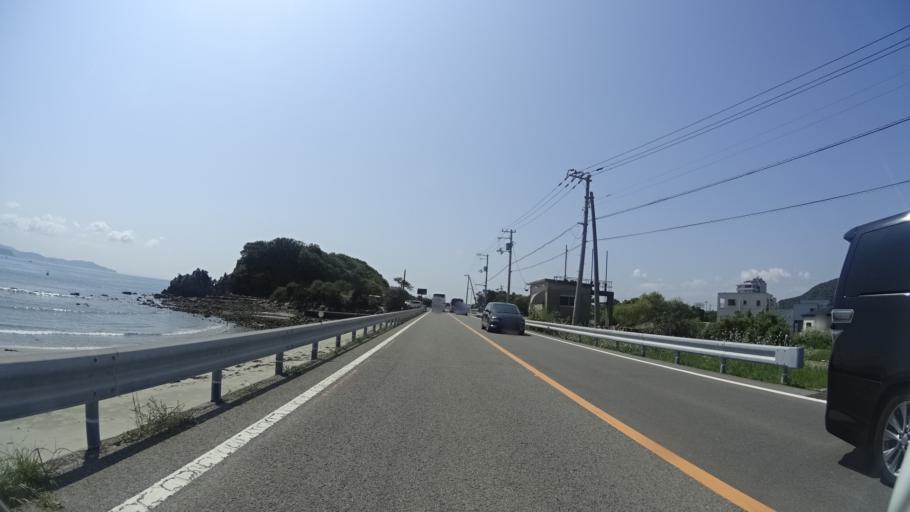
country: JP
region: Tokushima
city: Narutocho-mitsuishi
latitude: 34.2261
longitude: 134.6361
